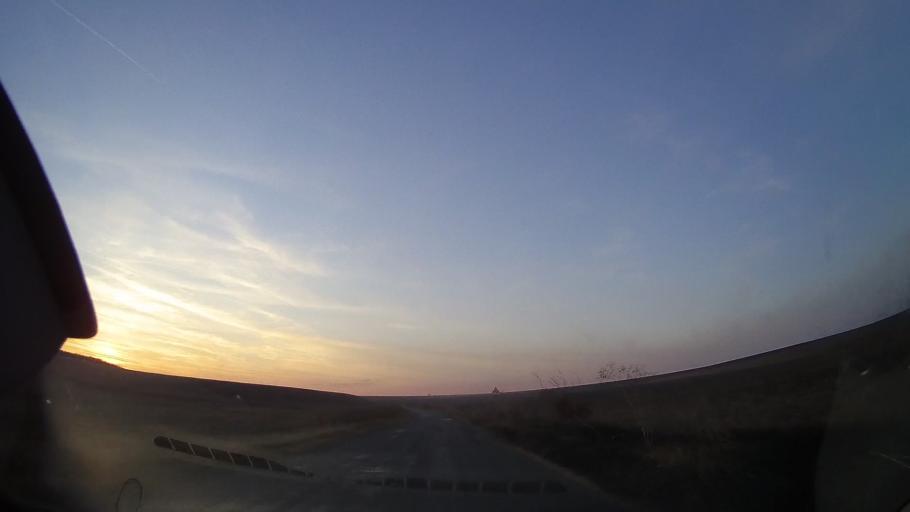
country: RO
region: Constanta
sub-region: Comuna Mereni
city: Mereni
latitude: 44.0184
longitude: 28.2987
